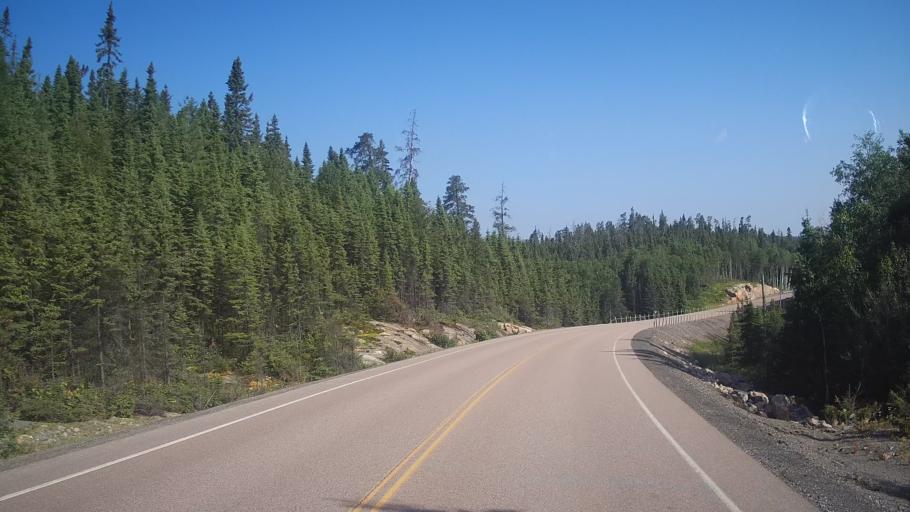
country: CA
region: Ontario
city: Rayside-Balfour
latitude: 47.0226
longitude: -81.6397
